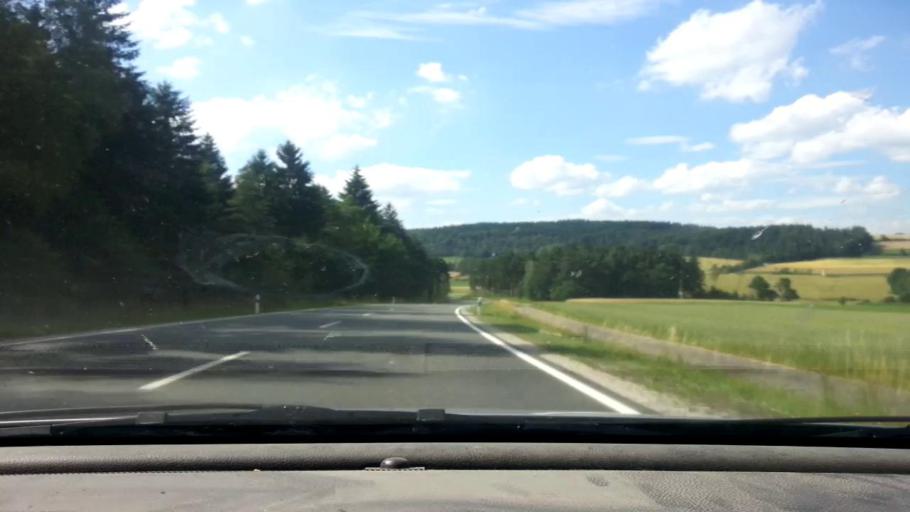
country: DE
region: Bavaria
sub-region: Upper Palatinate
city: Erbendorf
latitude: 49.8458
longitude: 11.9991
